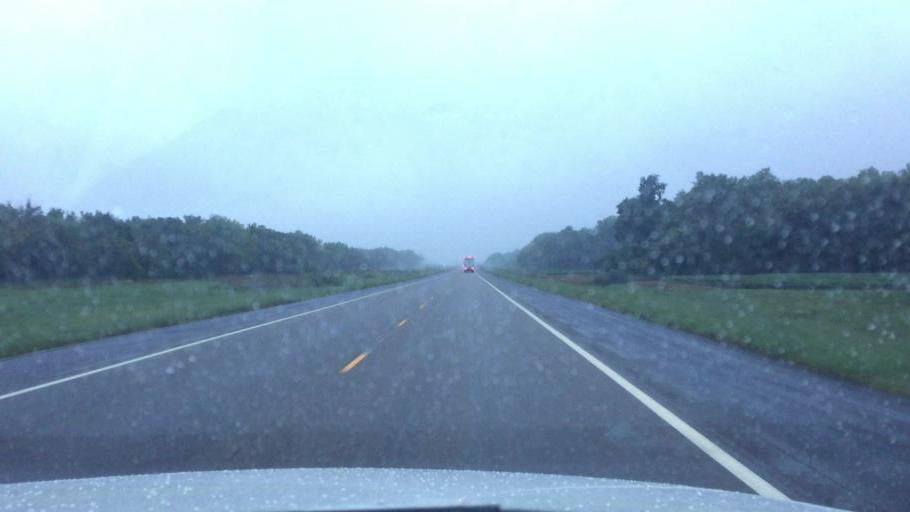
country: US
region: Kansas
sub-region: Montgomery County
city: Cherryvale
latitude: 37.4174
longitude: -95.4963
